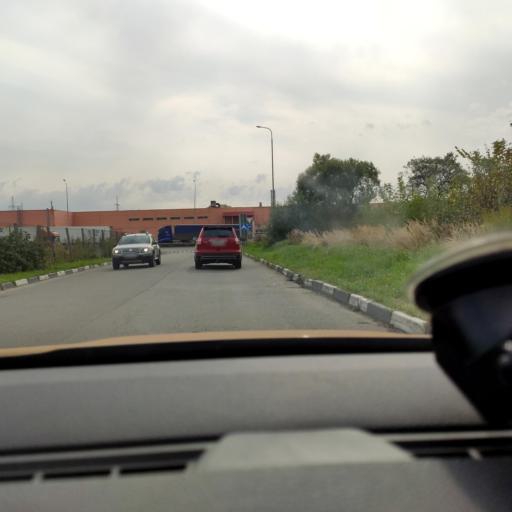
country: RU
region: Moscow
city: Vagonoremont
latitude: 55.9150
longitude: 37.5688
